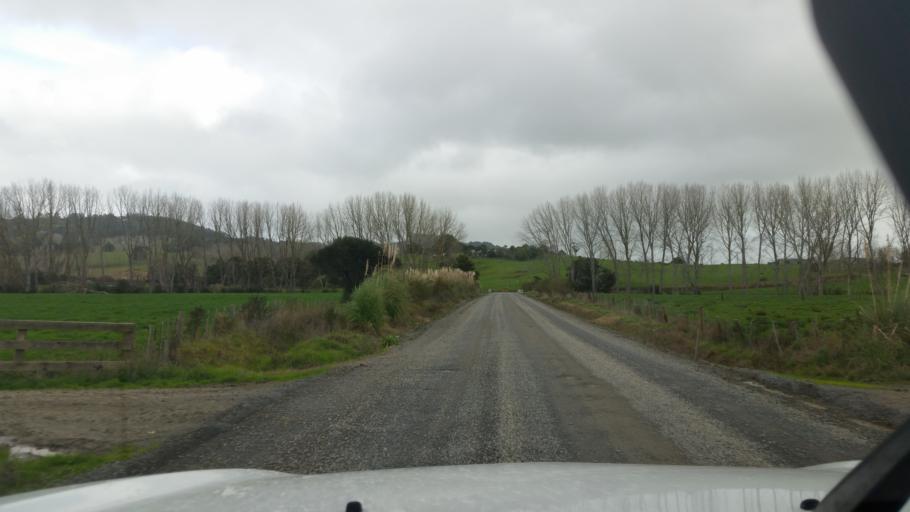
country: NZ
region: Northland
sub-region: Whangarei
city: Maungatapere
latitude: -35.6274
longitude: 174.1970
